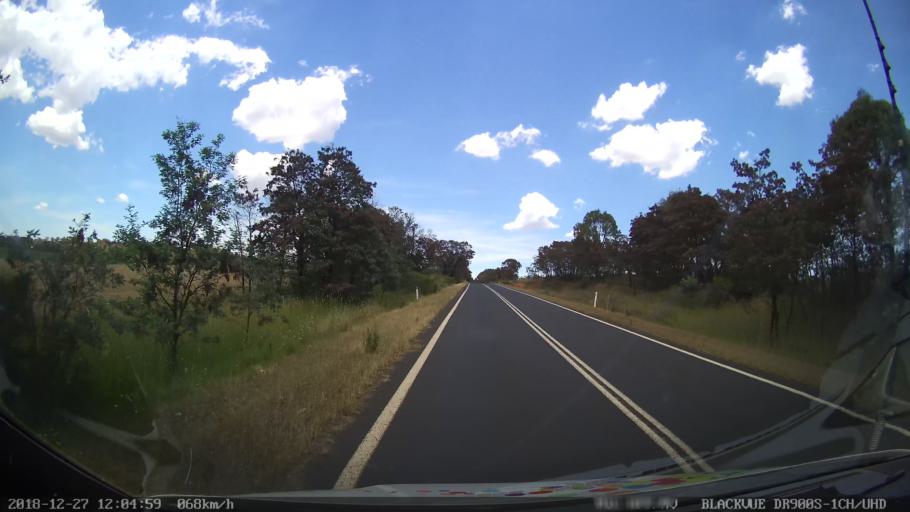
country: AU
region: New South Wales
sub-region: Blayney
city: Blayney
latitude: -33.7997
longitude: 149.3435
